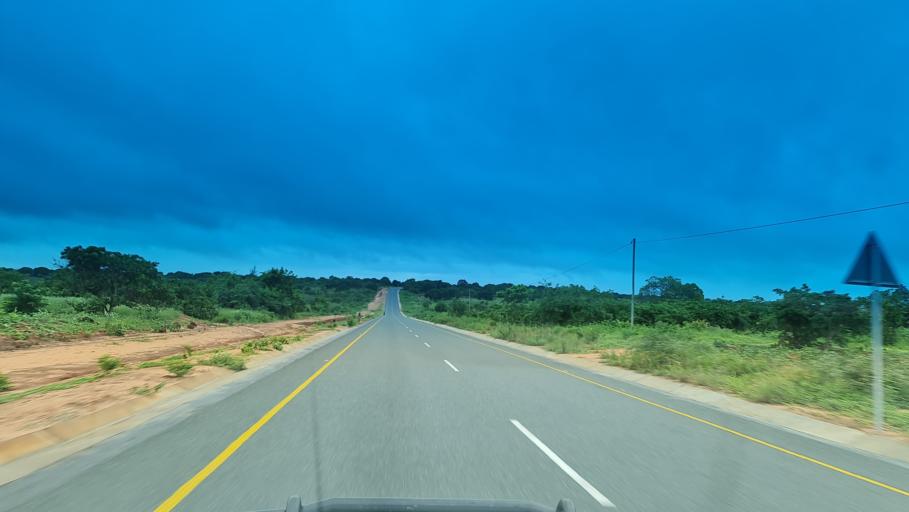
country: MZ
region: Nampula
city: Nampula
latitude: -15.6092
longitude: 39.3295
